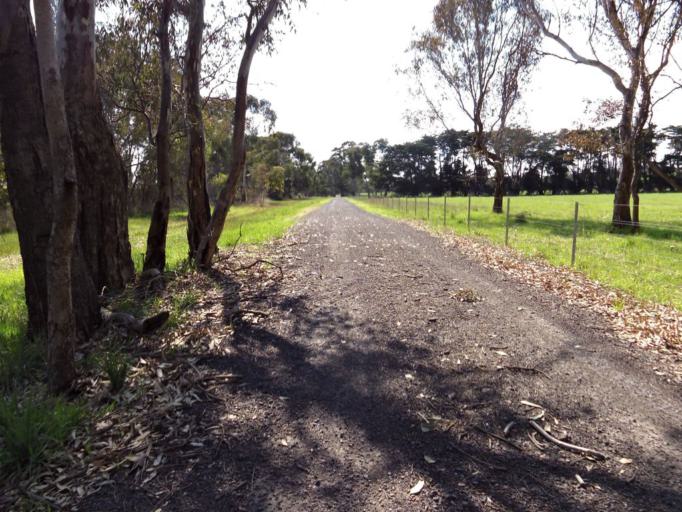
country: AU
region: Victoria
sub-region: Murrindindi
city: Alexandra
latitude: -37.1252
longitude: 145.5989
